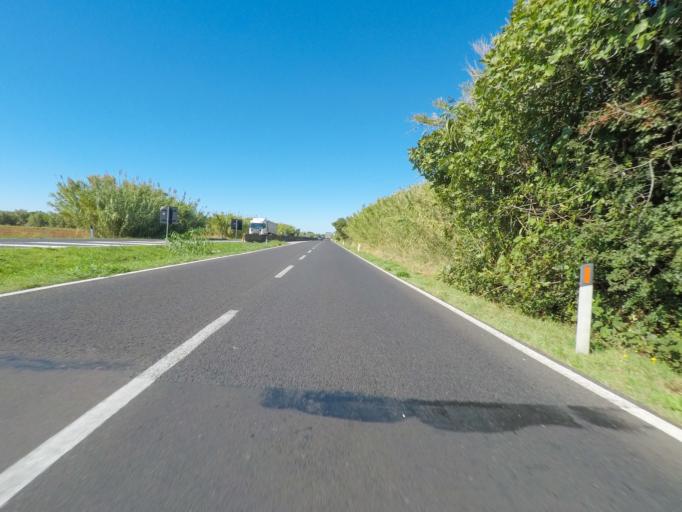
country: IT
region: Tuscany
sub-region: Provincia di Grosseto
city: Orbetello Scalo
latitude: 42.4566
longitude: 11.2495
